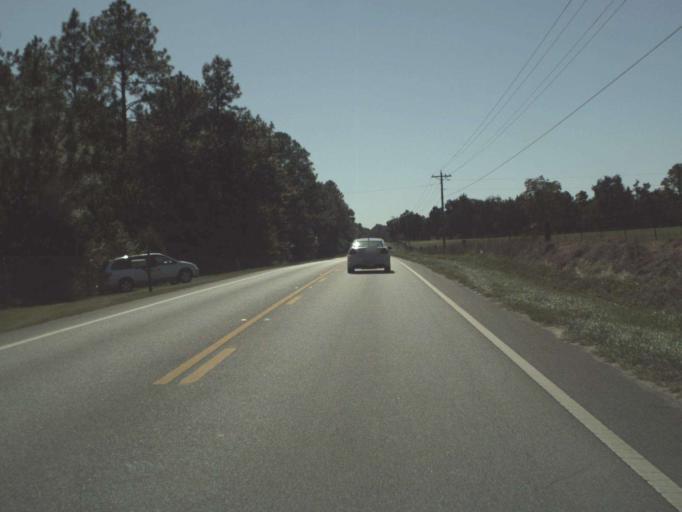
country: US
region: Florida
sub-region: Walton County
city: DeFuniak Springs
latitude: 30.8007
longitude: -86.1228
